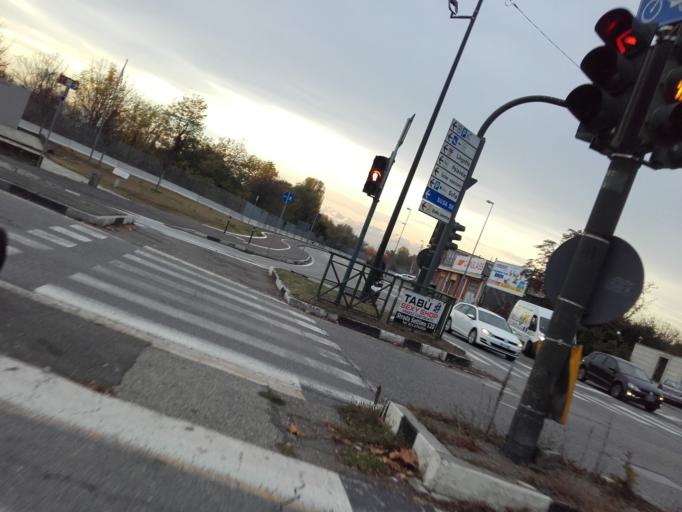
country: IT
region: Piedmont
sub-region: Provincia di Torino
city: San Mauro Torinese
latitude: 45.0990
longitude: 7.7226
